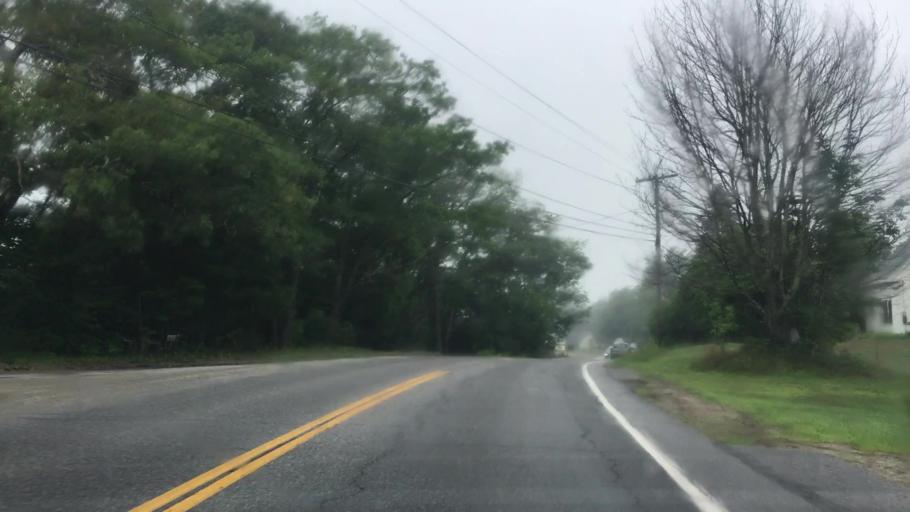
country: US
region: Maine
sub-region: Lincoln County
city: Edgecomb
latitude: 43.9622
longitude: -69.6295
